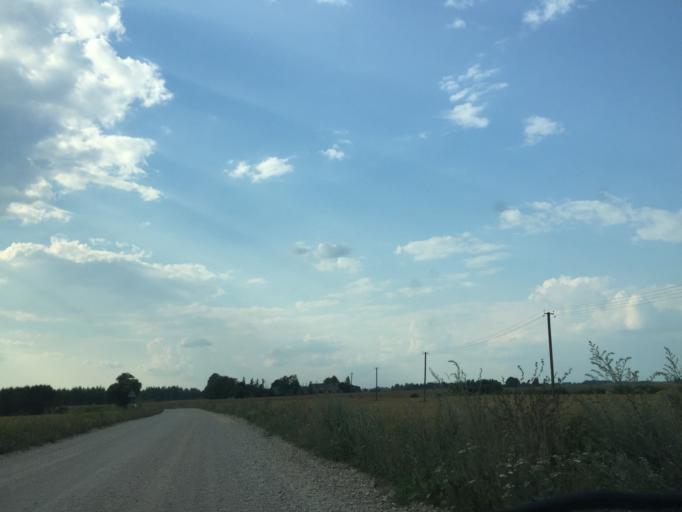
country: LT
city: Zagare
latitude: 56.4198
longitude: 23.1951
